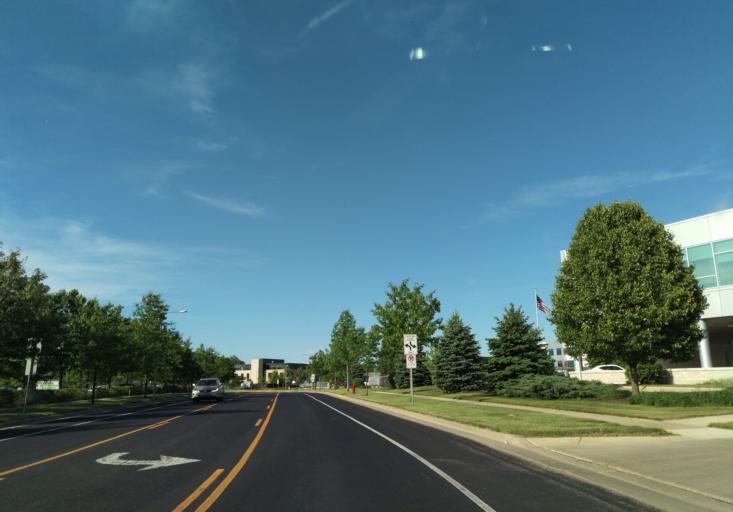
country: US
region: Wisconsin
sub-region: Dane County
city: Middleton
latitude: 43.0991
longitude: -89.5194
